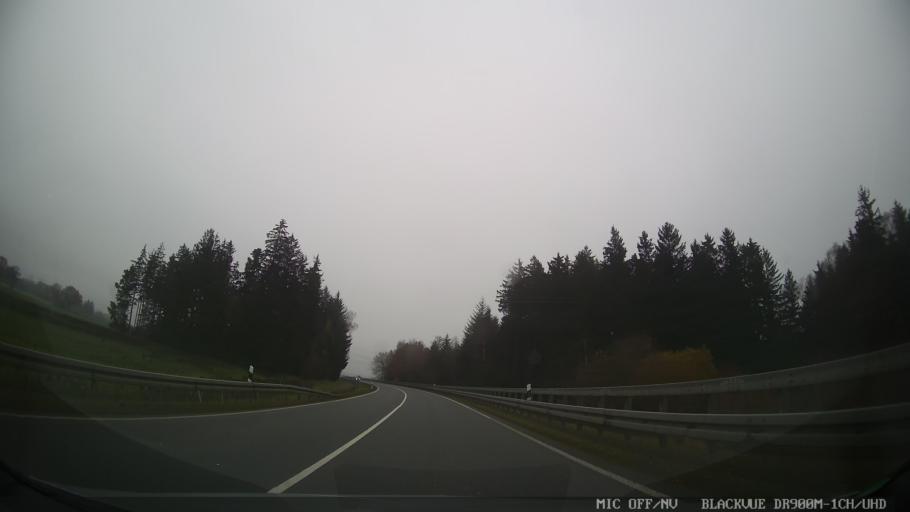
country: DE
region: Bavaria
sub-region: Upper Bavaria
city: Markt Schwaben
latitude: 48.2123
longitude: 11.8533
